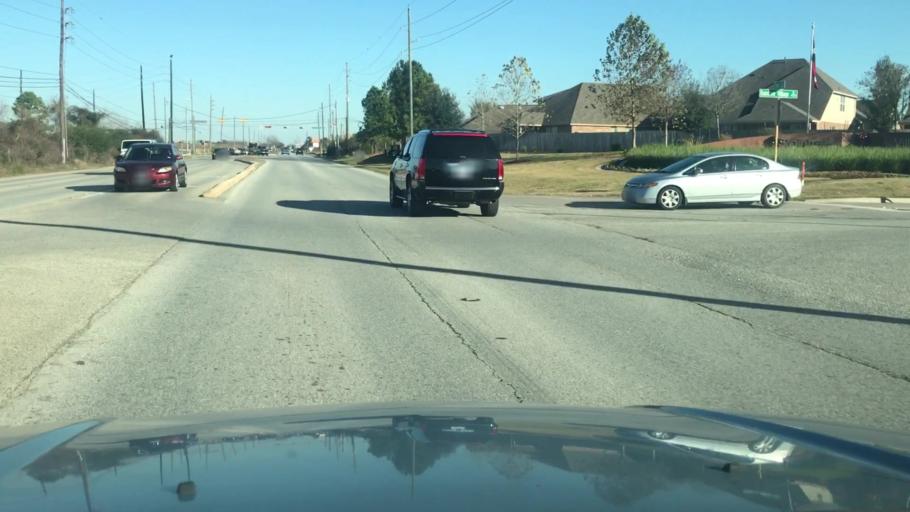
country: US
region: Texas
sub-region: Fort Bend County
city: Cinco Ranch
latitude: 29.8312
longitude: -95.7314
